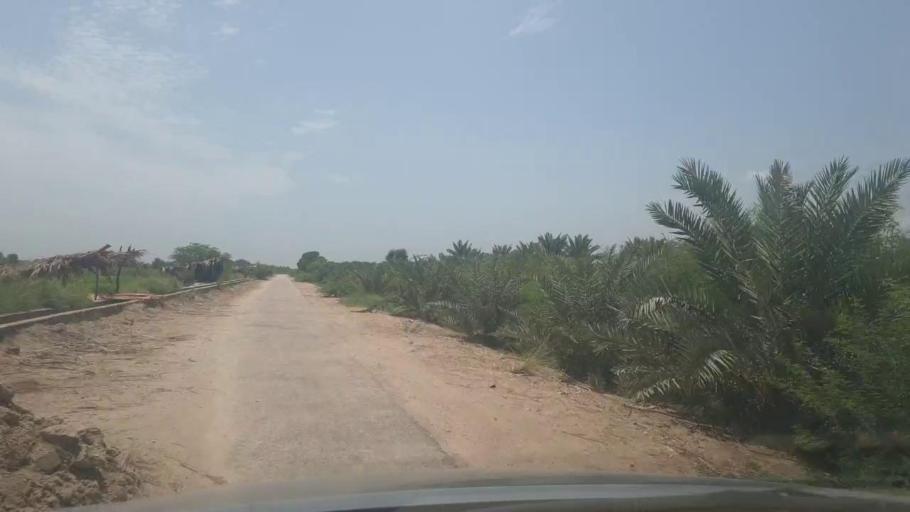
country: PK
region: Sindh
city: Kot Diji
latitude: 27.4078
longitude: 68.7305
